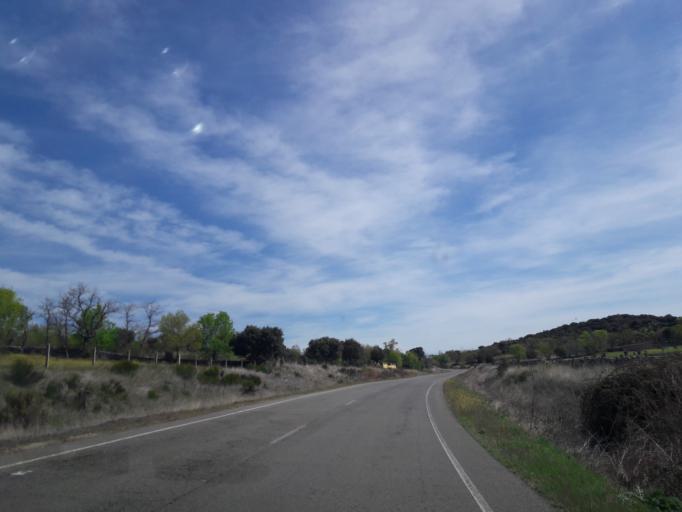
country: ES
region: Castille and Leon
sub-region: Provincia de Salamanca
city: Fuentes de Bejar
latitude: 40.5005
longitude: -5.7061
